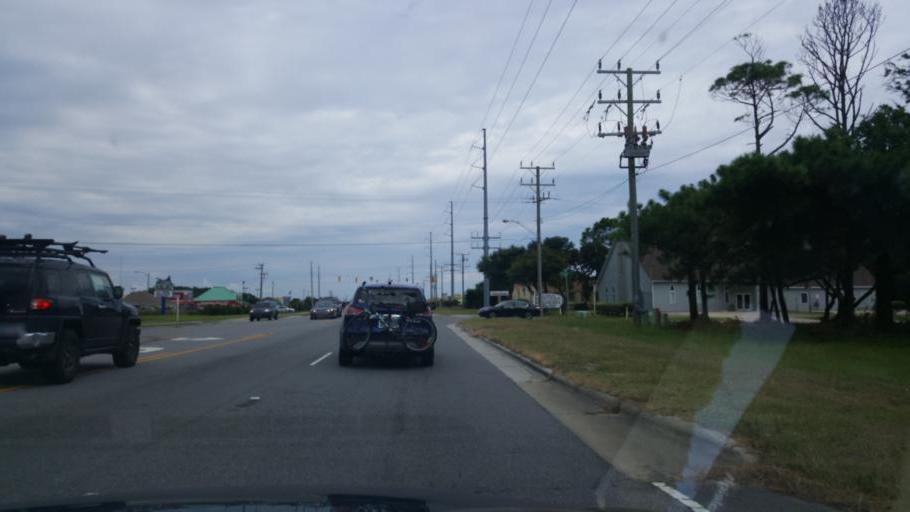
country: US
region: North Carolina
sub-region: Dare County
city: Nags Head
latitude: 35.9885
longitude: -75.6460
